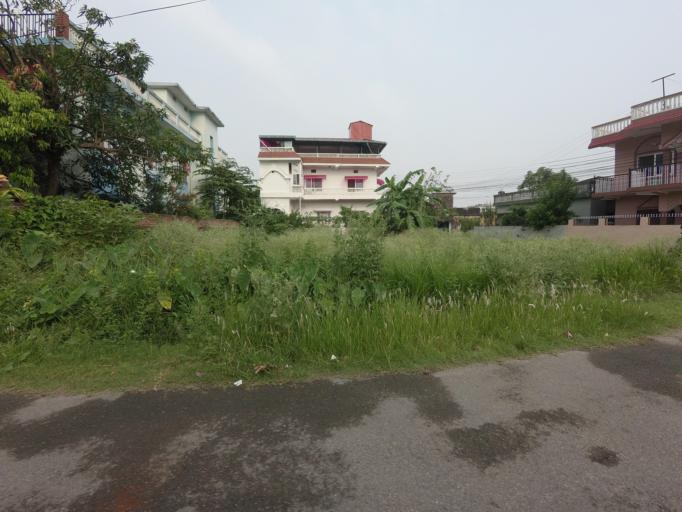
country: NP
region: Western Region
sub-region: Lumbini Zone
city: Bhairahawa
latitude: 27.5207
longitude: 83.4520
